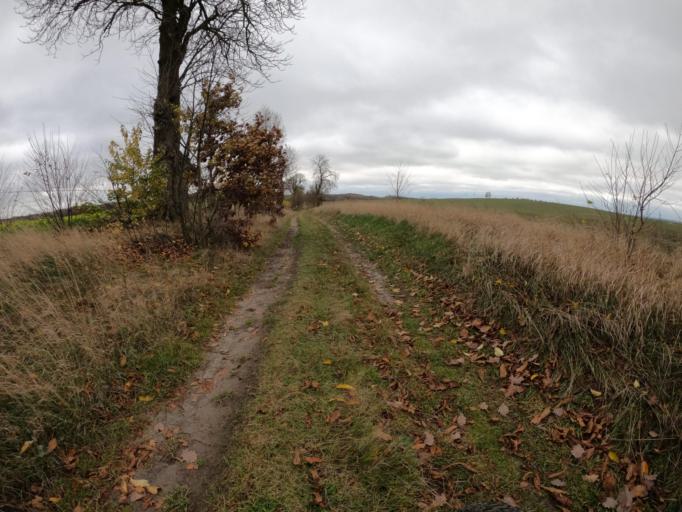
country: PL
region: West Pomeranian Voivodeship
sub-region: Powiat walecki
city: Tuczno
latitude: 53.2473
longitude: 16.2063
